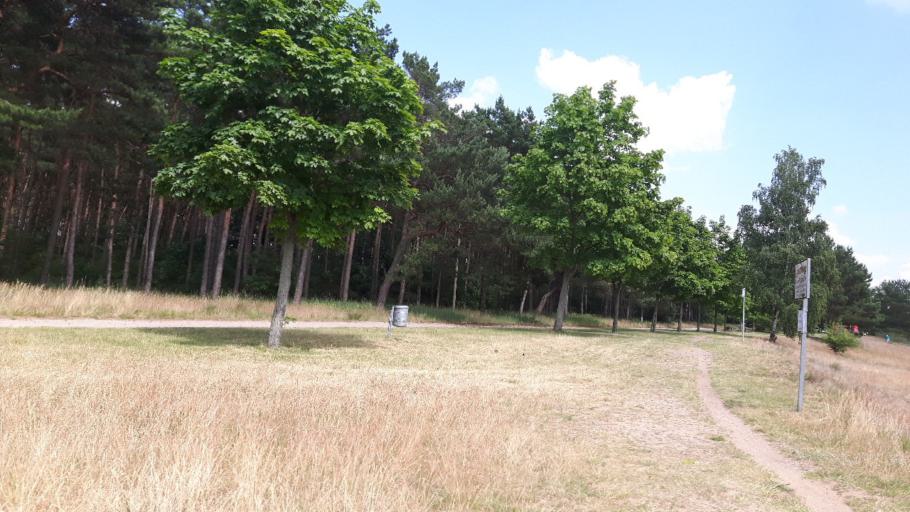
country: DE
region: Saxony-Anhalt
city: Bergwitz
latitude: 51.7932
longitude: 12.5793
